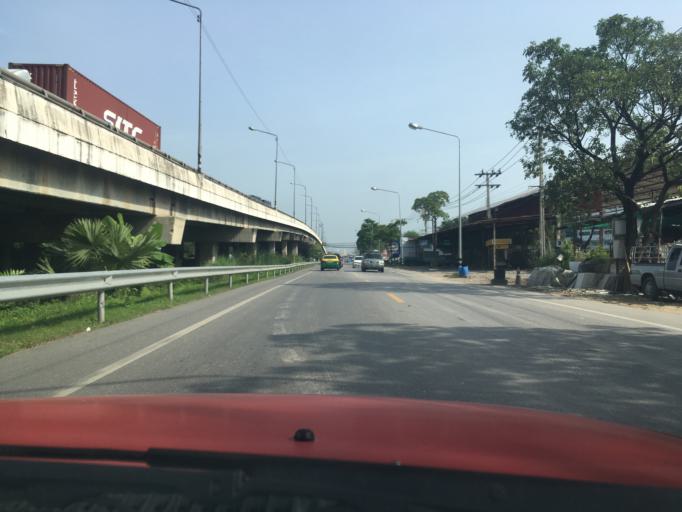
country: TH
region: Bangkok
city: Bang Khun Thian
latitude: 13.6334
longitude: 100.4160
